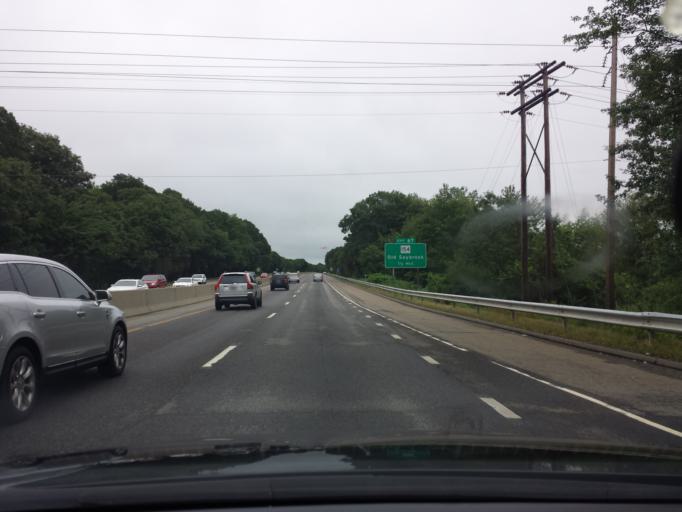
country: US
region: Connecticut
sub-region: Middlesex County
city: Old Saybrook
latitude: 41.3011
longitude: -72.3882
